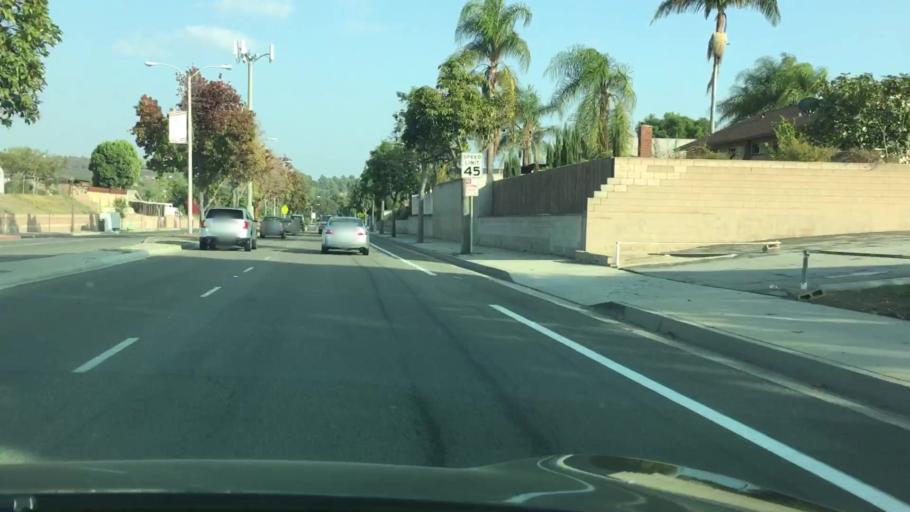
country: US
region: California
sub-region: Los Angeles County
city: La Mirada
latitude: 33.8987
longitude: -117.9959
